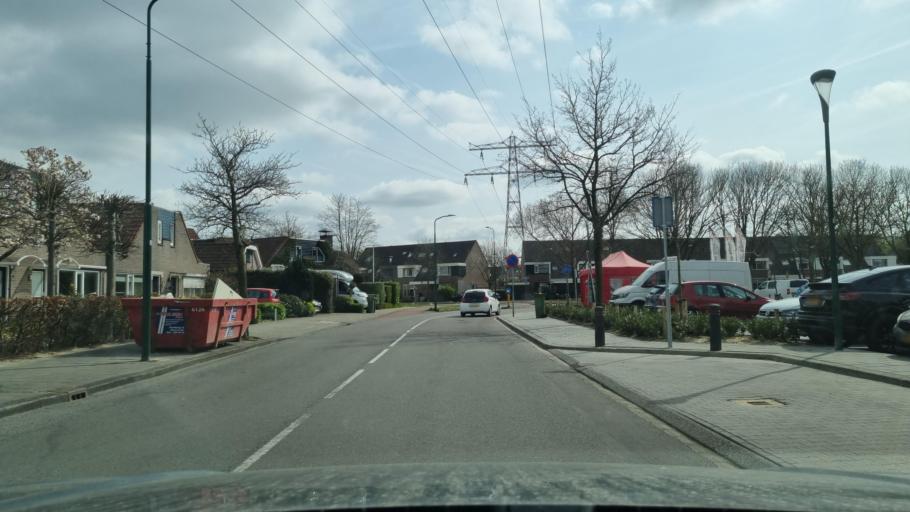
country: NL
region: Utrecht
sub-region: Gemeente Veenendaal
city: Veenendaal
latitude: 52.0290
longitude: 5.5332
